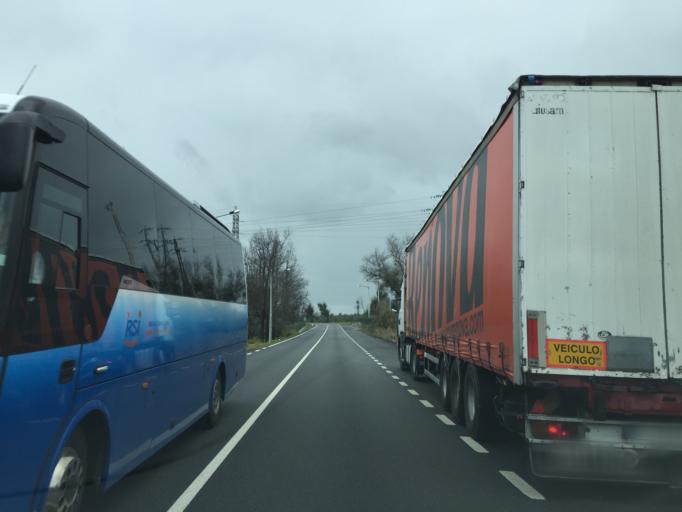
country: PT
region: Coimbra
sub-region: Tabua
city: Tabua
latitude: 40.3291
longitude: -7.9472
